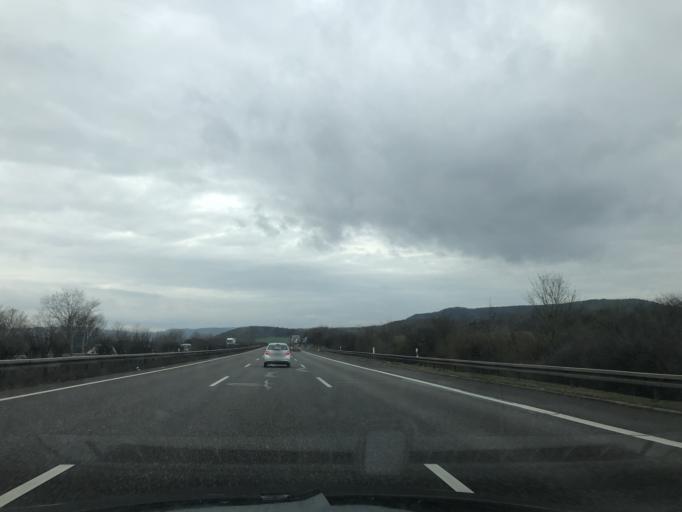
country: DE
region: Thuringia
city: Rausdorf
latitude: 50.8770
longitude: 11.6900
